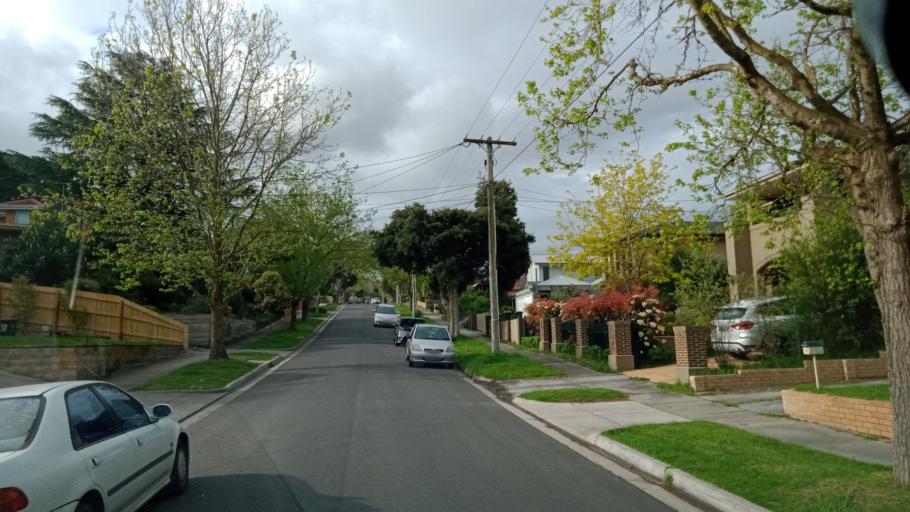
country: AU
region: Victoria
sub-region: Monash
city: Notting Hill
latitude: -37.8810
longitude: 145.1552
